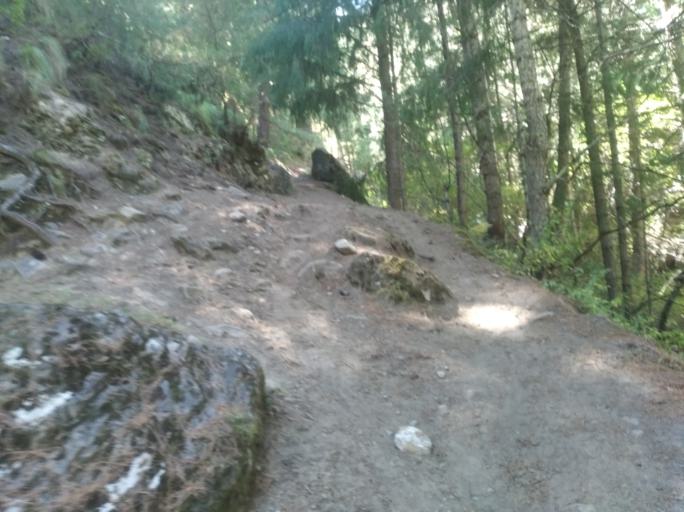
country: NP
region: Western Region
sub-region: Dhawalagiri Zone
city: Jomsom
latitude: 28.8865
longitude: 83.0688
